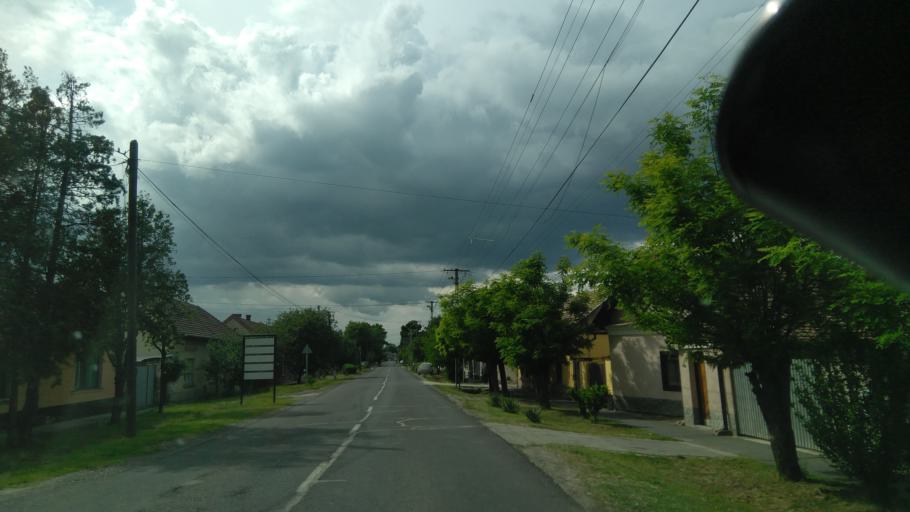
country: HU
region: Bekes
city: Oroshaza
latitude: 46.5684
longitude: 20.6576
